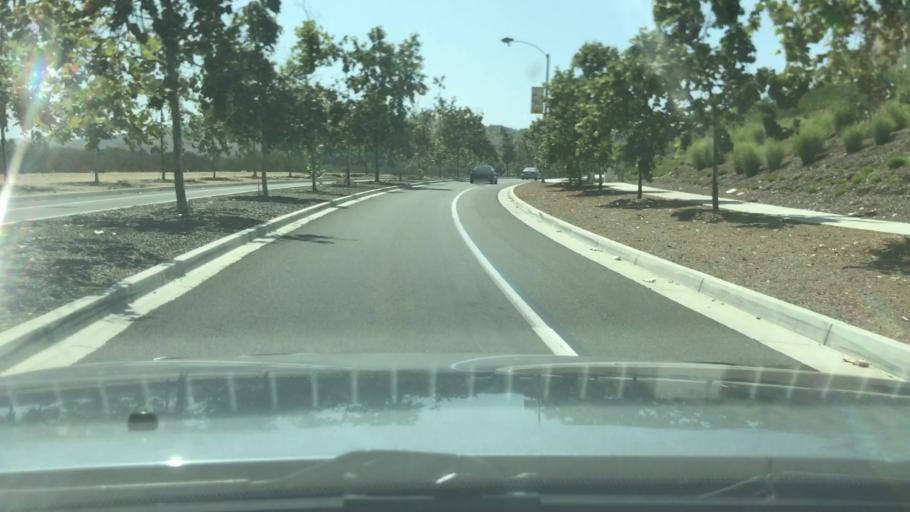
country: US
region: California
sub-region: Orange County
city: San Joaquin Hills
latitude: 33.6377
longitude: -117.8285
